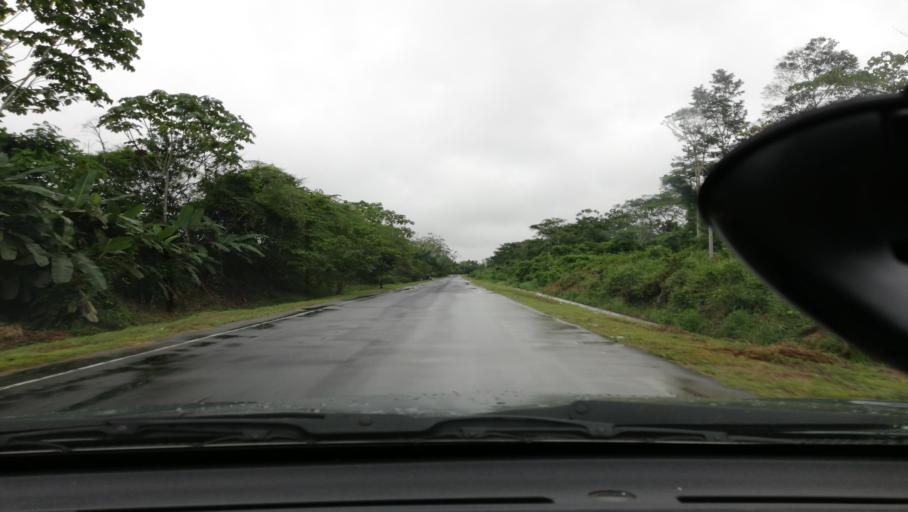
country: PE
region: Loreto
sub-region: Provincia de Maynas
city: San Juan
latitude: -4.0405
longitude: -73.4369
